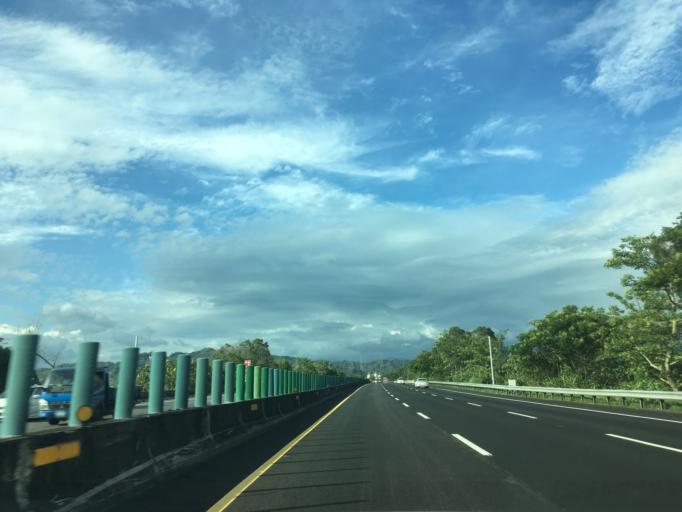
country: TW
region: Taiwan
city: Lugu
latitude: 23.8152
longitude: 120.7006
